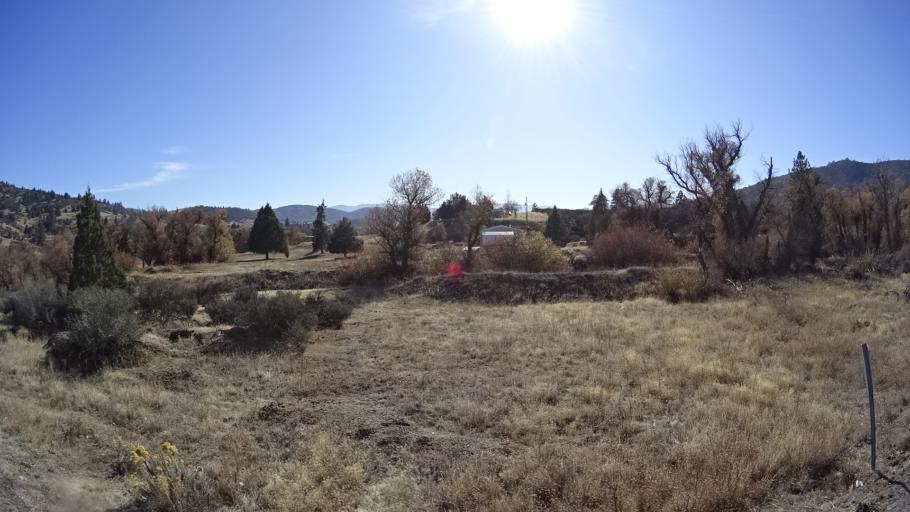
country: US
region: California
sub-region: Siskiyou County
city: Yreka
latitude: 41.7597
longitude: -122.6263
